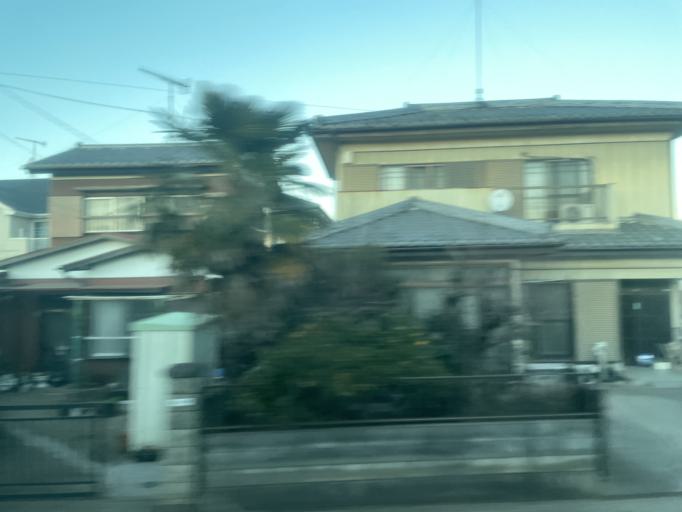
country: JP
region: Saitama
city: Fukayacho
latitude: 36.1961
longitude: 139.2596
